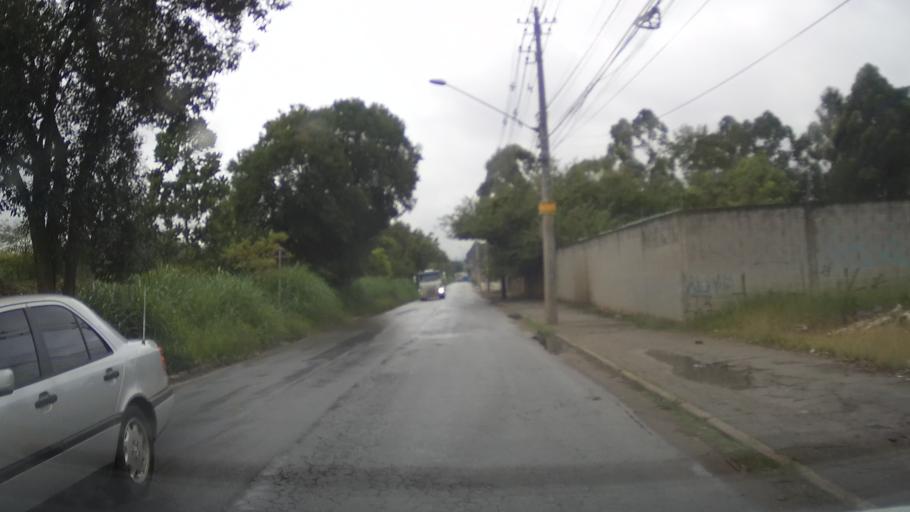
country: BR
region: Sao Paulo
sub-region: Guarulhos
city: Guarulhos
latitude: -23.4762
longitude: -46.4589
